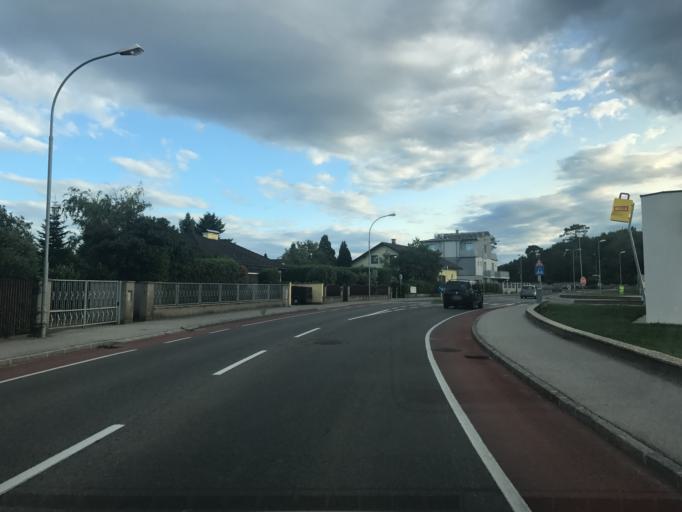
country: AT
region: Lower Austria
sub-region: Wiener Neustadt Stadt
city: Wiener Neustadt
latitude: 47.8092
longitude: 16.2601
